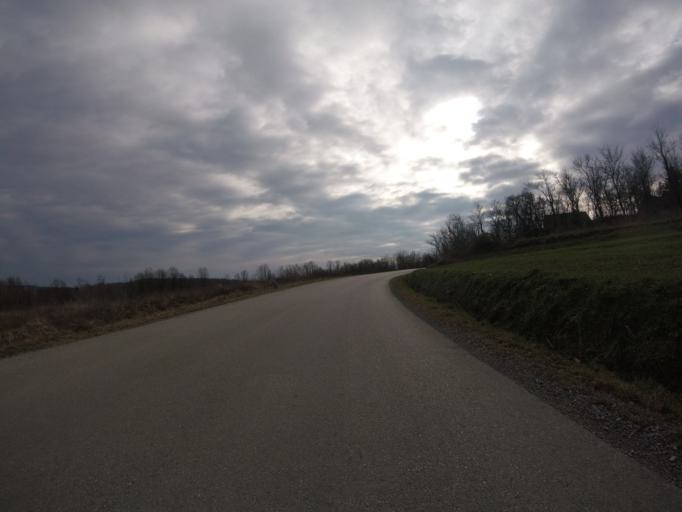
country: HR
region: Zagrebacka
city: Mraclin
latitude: 45.5151
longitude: 16.0544
